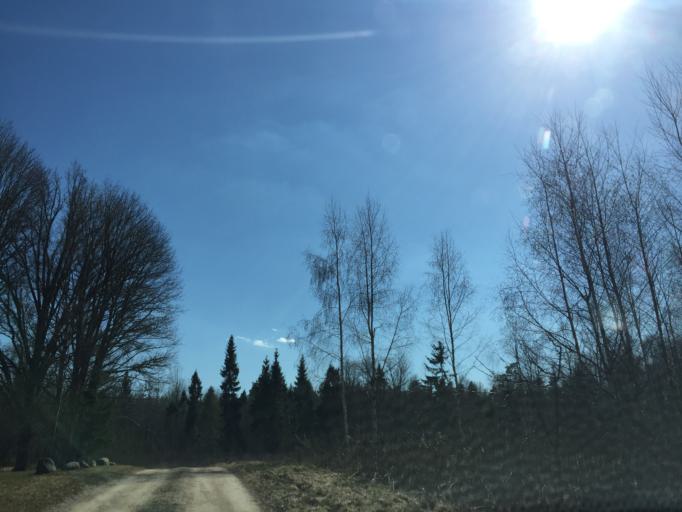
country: EE
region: Viljandimaa
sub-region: Viljandi linn
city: Viljandi
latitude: 58.2743
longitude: 25.6045
